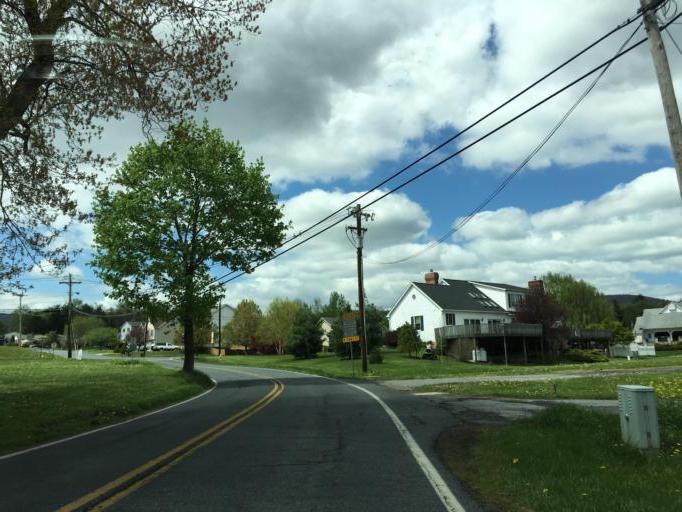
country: US
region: Maryland
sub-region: Frederick County
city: Thurmont
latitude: 39.6300
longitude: -77.3960
